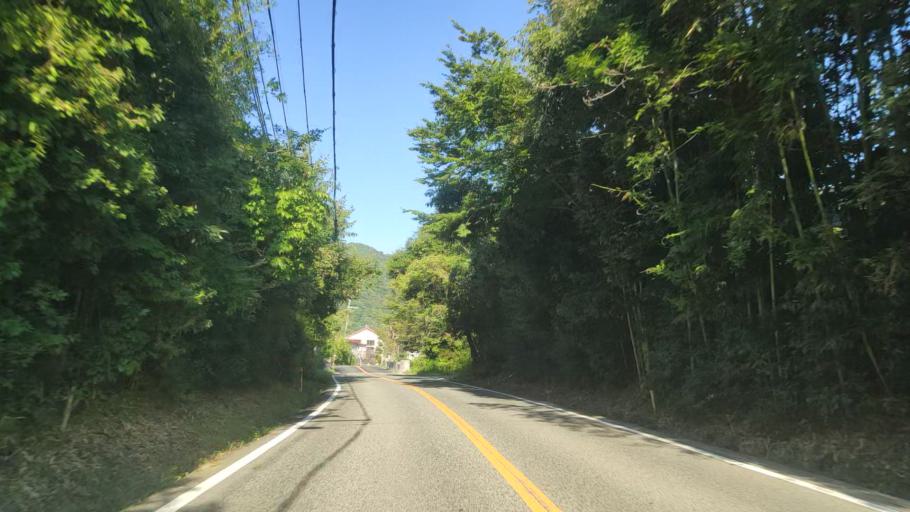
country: JP
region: Hyogo
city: Sandacho
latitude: 34.7976
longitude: 135.2252
